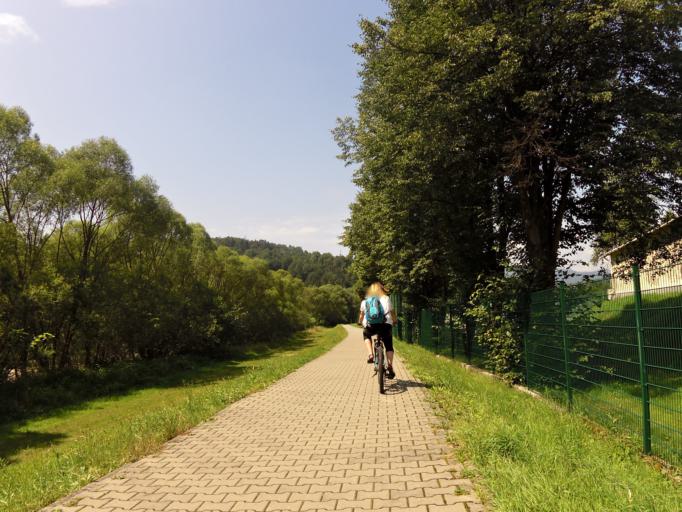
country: PL
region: Silesian Voivodeship
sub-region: Powiat zywiecki
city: Milowka
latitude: 49.5537
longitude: 19.0868
